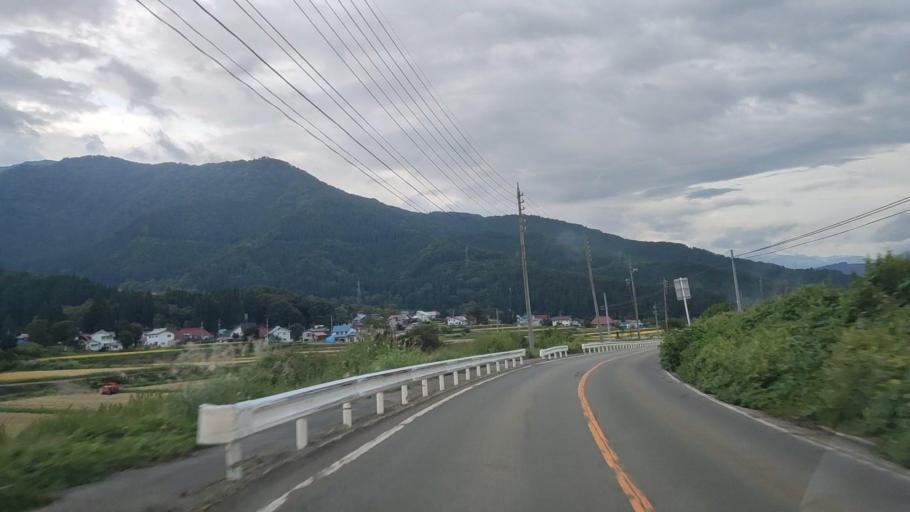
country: JP
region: Nagano
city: Iiyama
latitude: 36.8850
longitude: 138.4117
